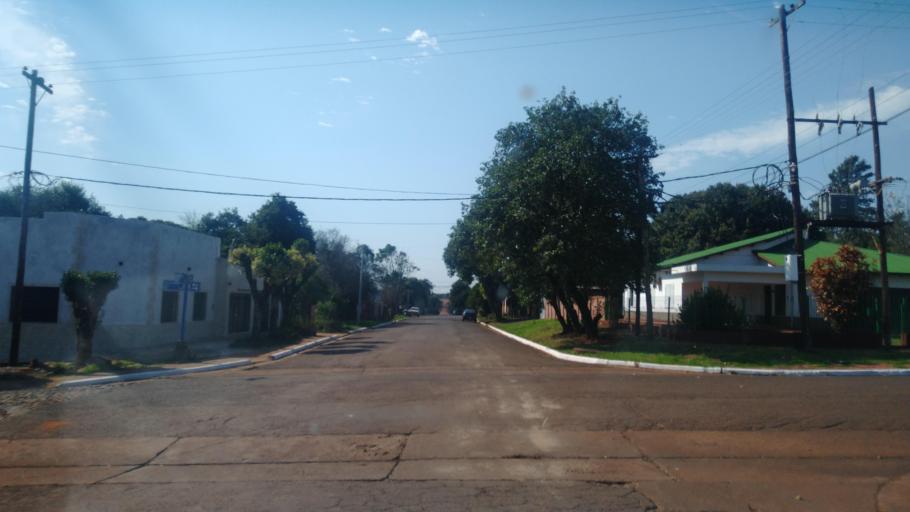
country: AR
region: Misiones
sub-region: Departamento de San Ignacio
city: San Ignacio
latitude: -27.2537
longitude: -55.5363
